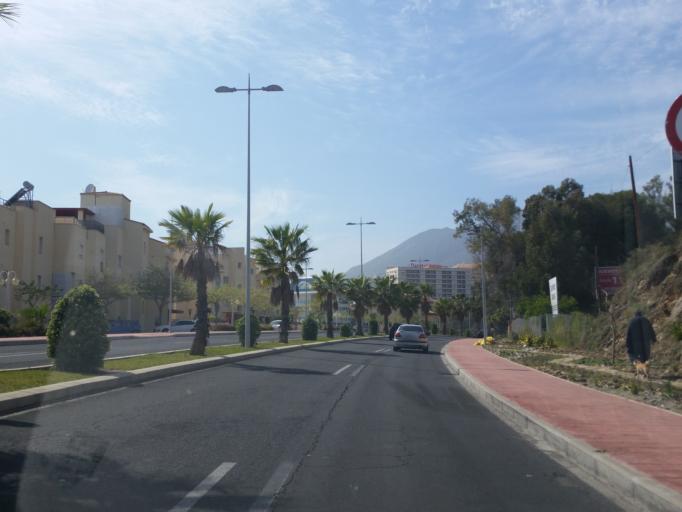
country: ES
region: Andalusia
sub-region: Provincia de Malaga
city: Benalmadena
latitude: 36.5805
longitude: -4.5453
